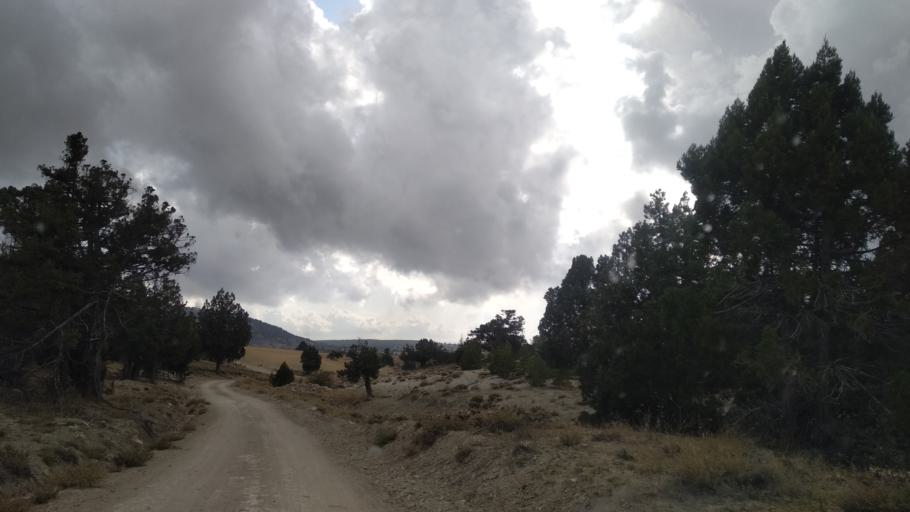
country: TR
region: Mersin
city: Sarikavak
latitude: 36.5732
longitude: 33.7524
